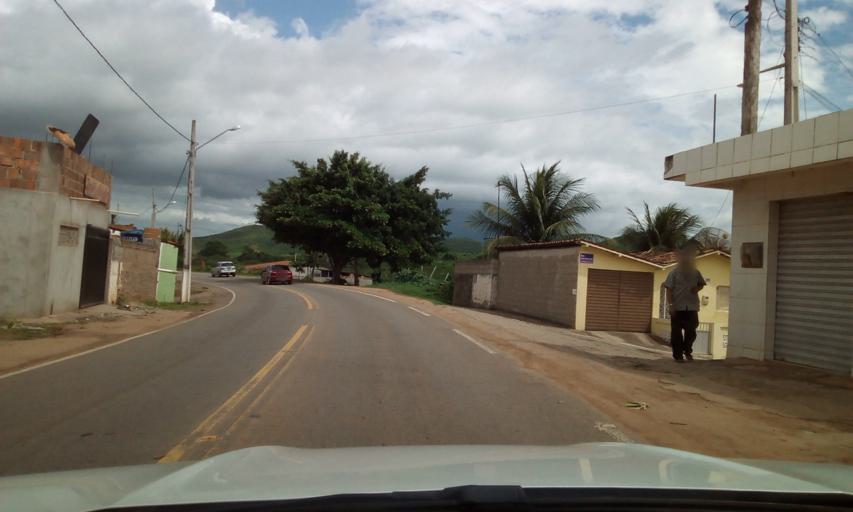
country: BR
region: Paraiba
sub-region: Guarabira
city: Guarabira
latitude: -6.8960
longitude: -35.5253
